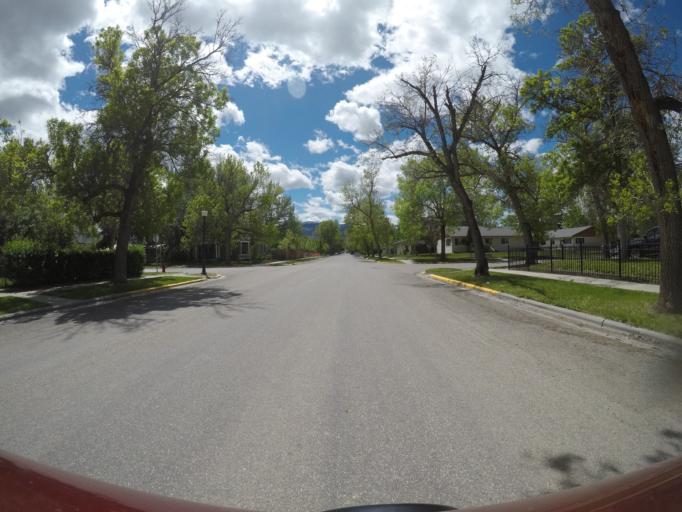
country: US
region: Montana
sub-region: Park County
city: Livingston
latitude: 45.6597
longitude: -110.5632
